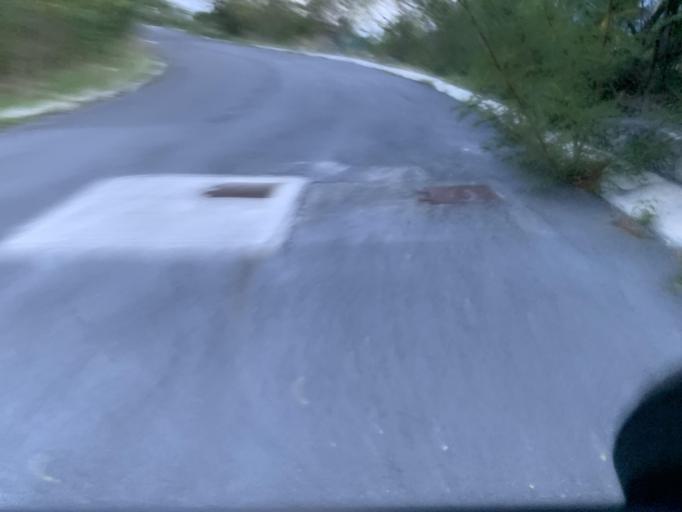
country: MX
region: Nuevo Leon
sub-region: Juarez
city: Bosques de San Pedro
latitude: 25.5192
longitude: -100.1854
